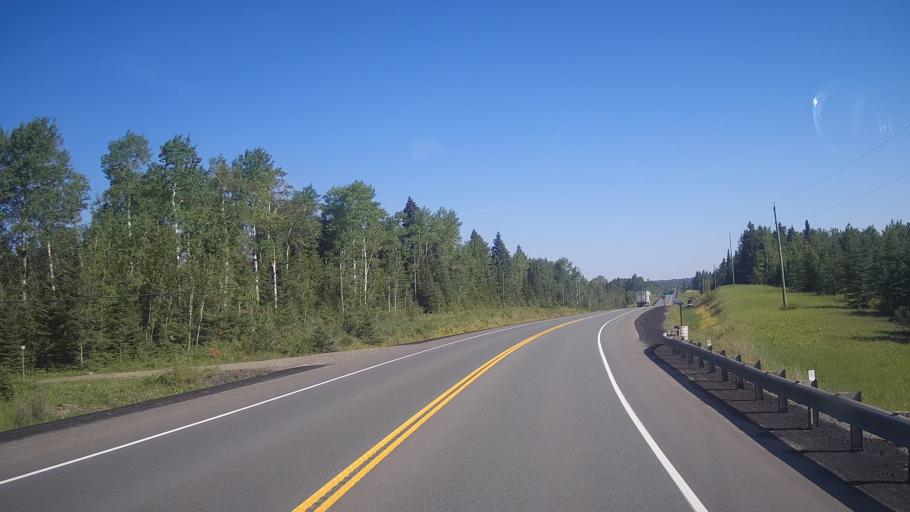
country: CA
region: Ontario
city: Dryden
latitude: 49.6712
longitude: -92.4924
